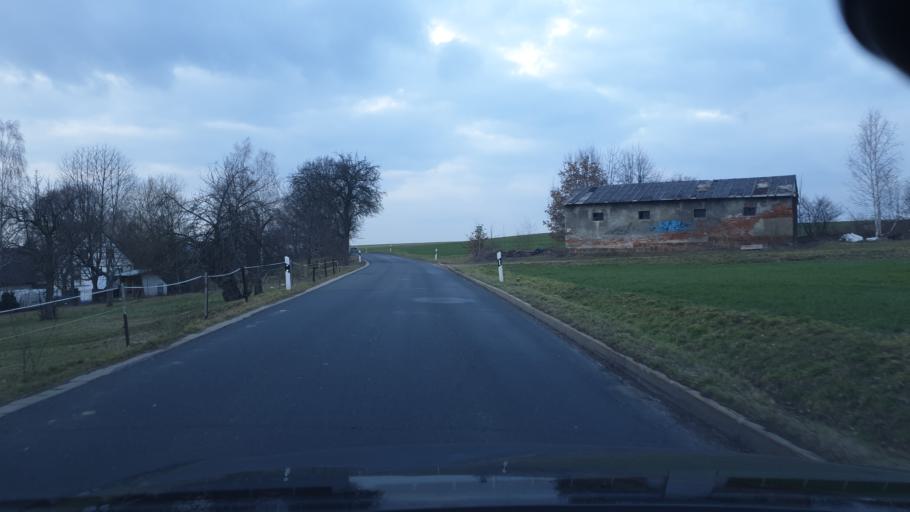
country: DE
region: Saxony
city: Erlau
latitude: 50.9890
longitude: 12.9285
